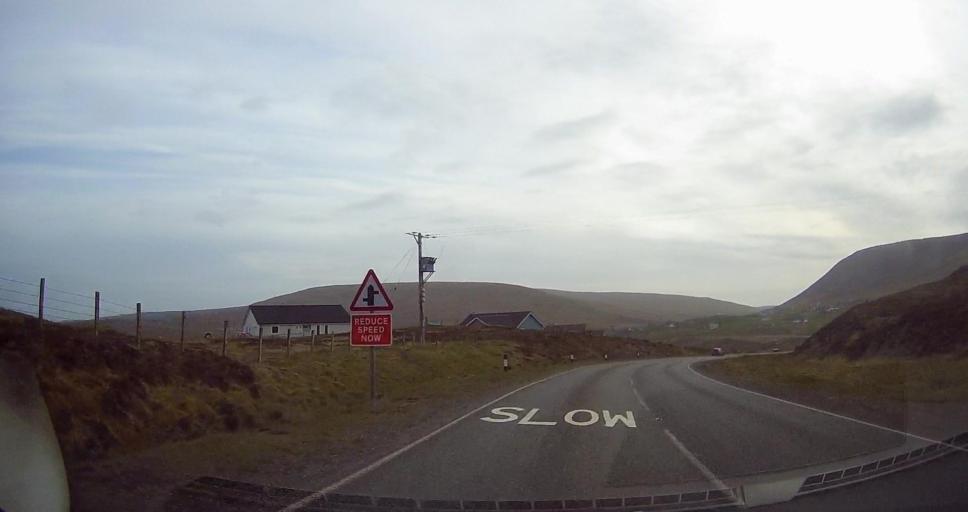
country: GB
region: Scotland
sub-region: Shetland Islands
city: Lerwick
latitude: 60.1051
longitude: -1.2201
